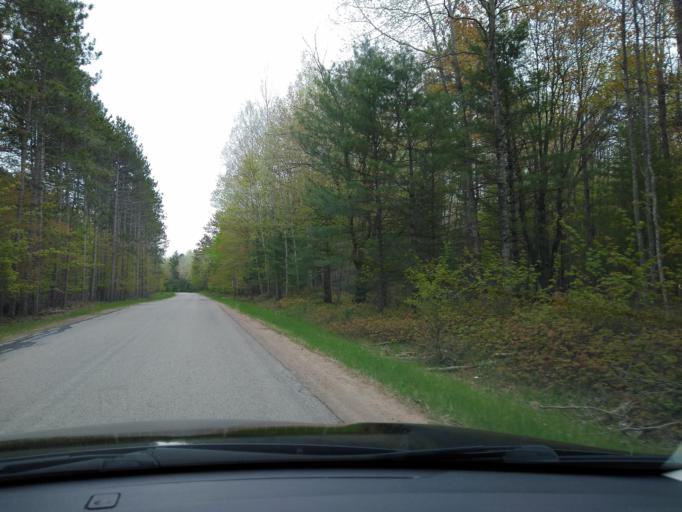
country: US
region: Michigan
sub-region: Delta County
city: Gladstone
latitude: 45.8909
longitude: -87.0497
